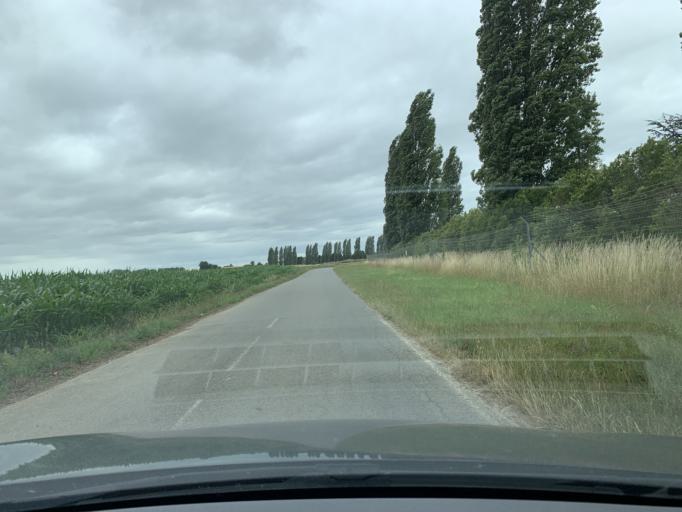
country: FR
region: Nord-Pas-de-Calais
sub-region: Departement du Pas-de-Calais
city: Oisy-le-Verger
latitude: 50.2138
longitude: 3.1377
